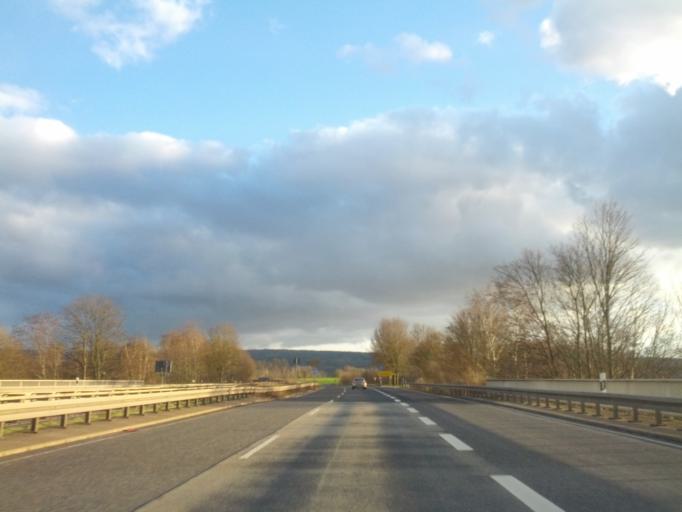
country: DE
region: Hesse
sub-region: Regierungsbezirk Kassel
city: Kaufungen
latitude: 51.2846
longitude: 9.5881
